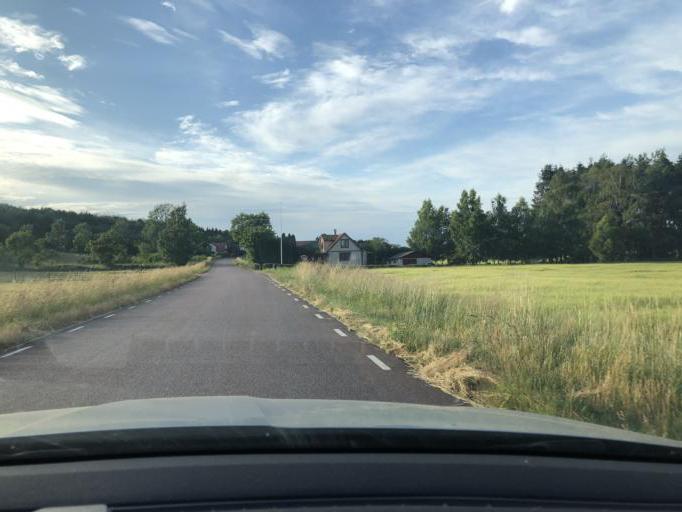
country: SE
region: Blekinge
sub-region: Solvesborgs Kommun
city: Soelvesborg
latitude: 56.1317
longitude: 14.6078
